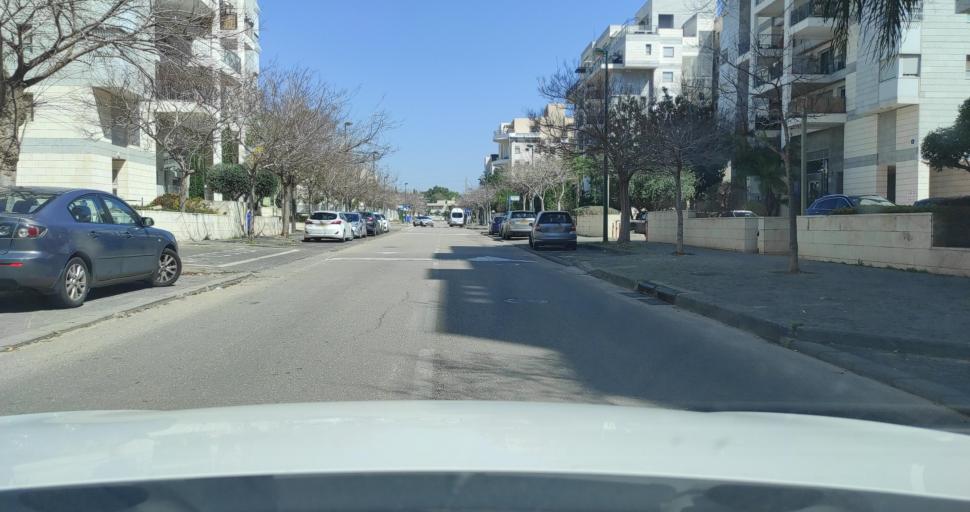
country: IL
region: Central District
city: Nordiyya
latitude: 32.2977
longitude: 34.8746
